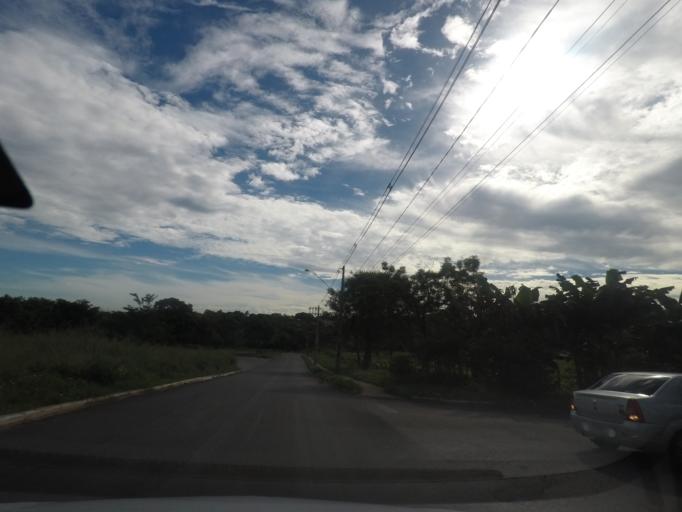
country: BR
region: Goias
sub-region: Aparecida De Goiania
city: Aparecida de Goiania
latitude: -16.8187
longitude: -49.3053
